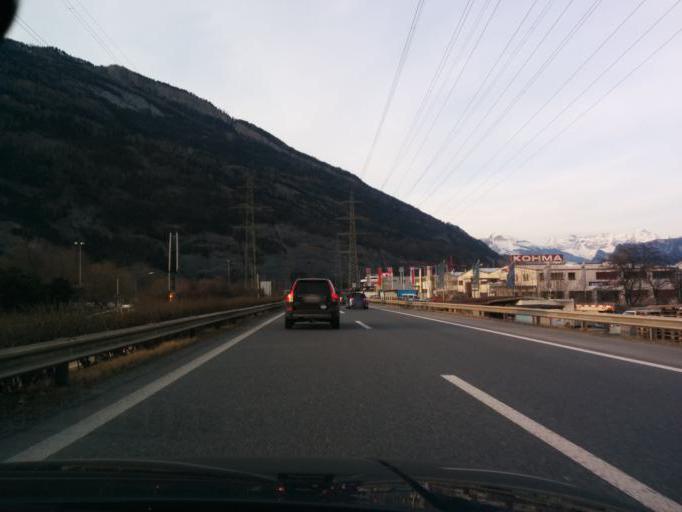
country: CH
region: Grisons
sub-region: Plessur District
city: Chur
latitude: 46.8535
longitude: 9.5068
